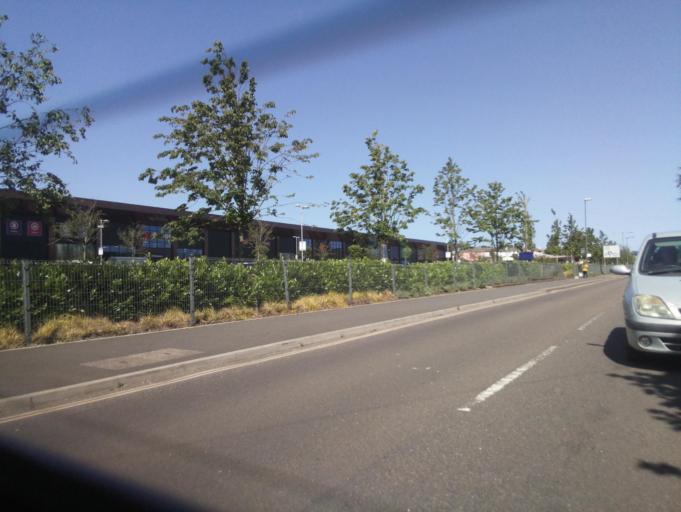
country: GB
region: England
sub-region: Borough of Torbay
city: Paignton
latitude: 50.4143
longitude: -3.5825
